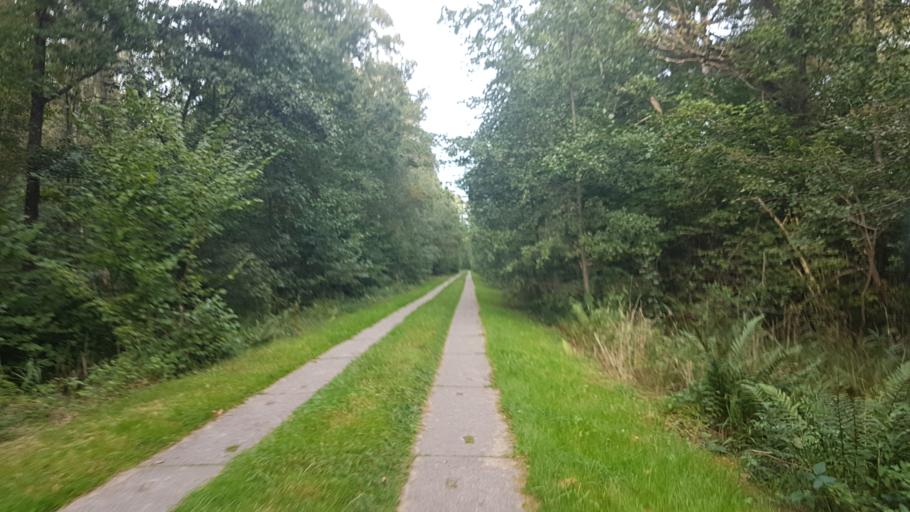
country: DE
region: Mecklenburg-Vorpommern
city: Gingst
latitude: 54.4793
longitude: 13.1785
